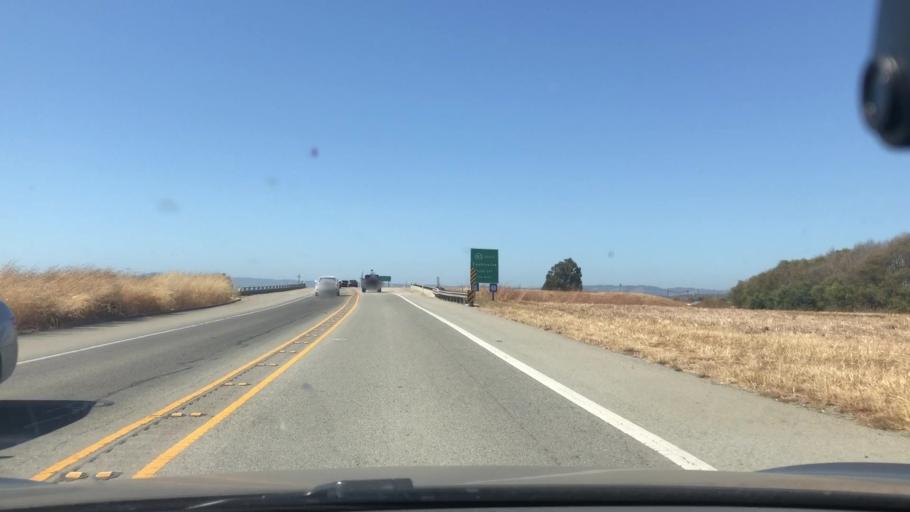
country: US
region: California
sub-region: Monterey County
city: Castroville
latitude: 36.7669
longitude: -121.7651
